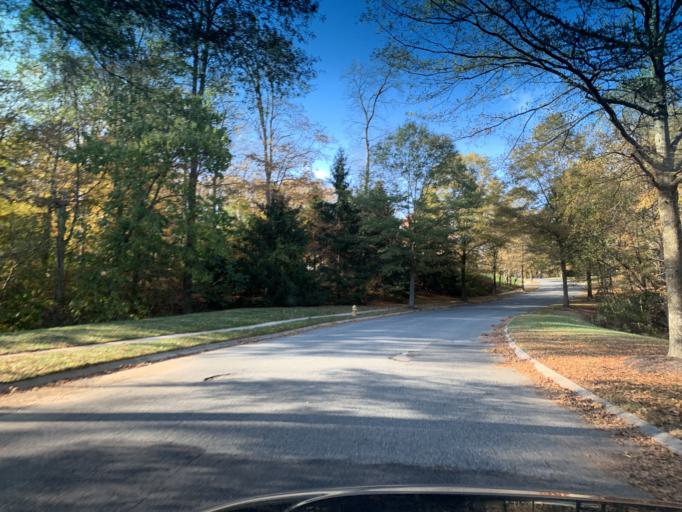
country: US
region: Maryland
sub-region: Harford County
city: Bel Air South
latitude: 39.5127
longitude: -76.3046
